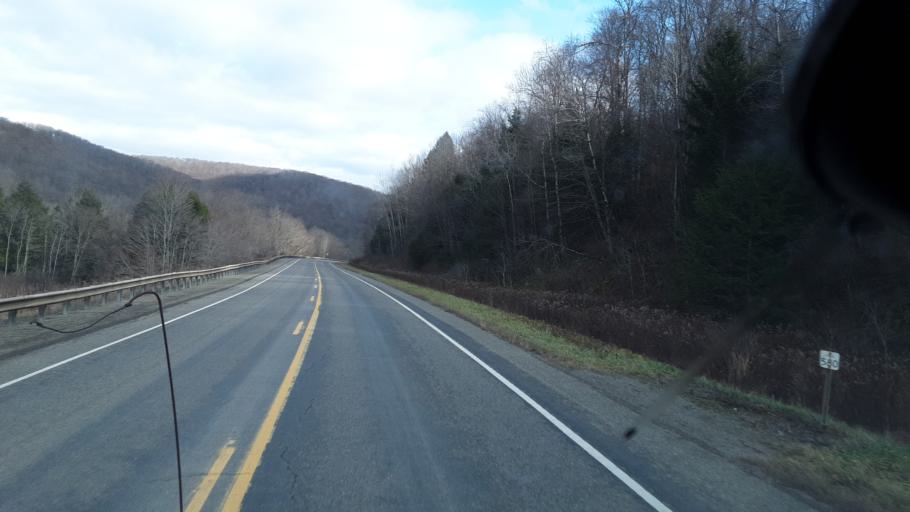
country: US
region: Pennsylvania
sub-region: Potter County
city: Galeton
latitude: 41.7862
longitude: -77.7930
